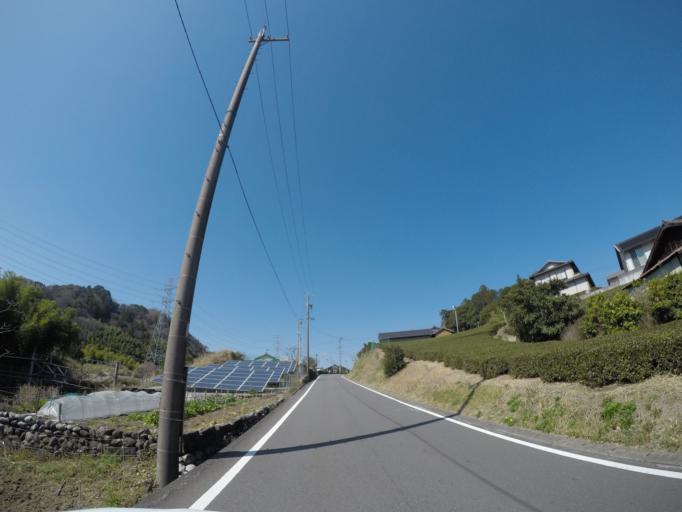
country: JP
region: Shizuoka
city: Kanaya
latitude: 34.7946
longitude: 138.1252
